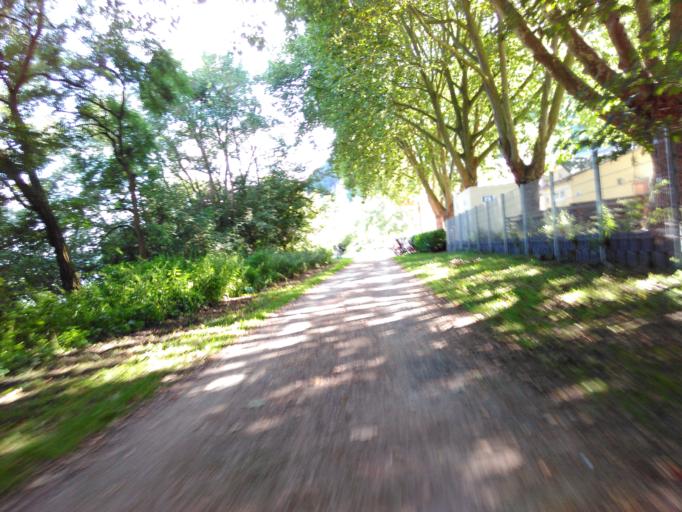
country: DE
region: Rheinland-Pfalz
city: Koblenz
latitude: 50.3236
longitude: 7.5871
